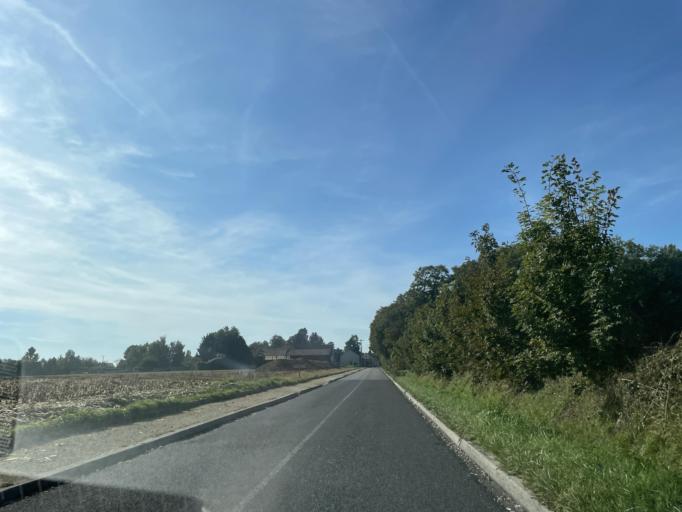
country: FR
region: Ile-de-France
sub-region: Departement de Seine-et-Marne
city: Saint-Jean-les-Deux-Jumeaux
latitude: 48.9458
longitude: 2.9905
